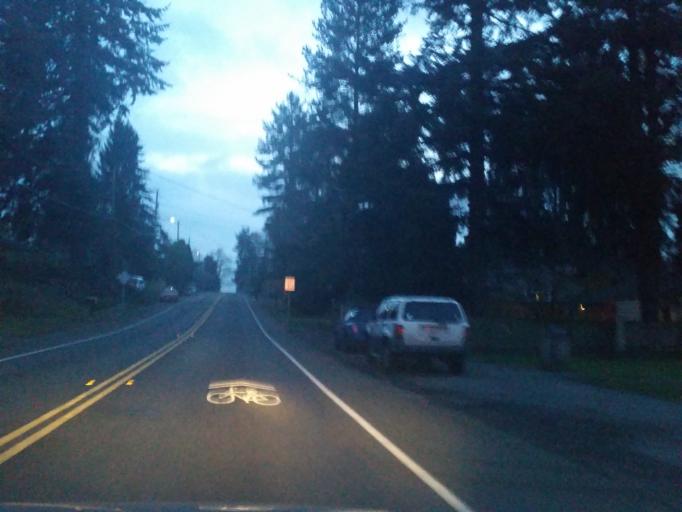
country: US
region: Washington
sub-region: King County
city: Shoreline
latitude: 47.7627
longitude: -122.3189
